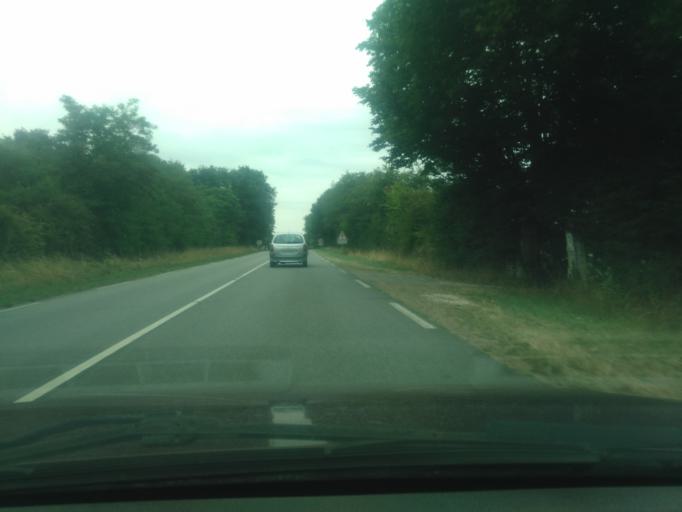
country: FR
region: Centre
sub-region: Departement de l'Indre
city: Le Blanc
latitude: 46.6225
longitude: 1.0353
